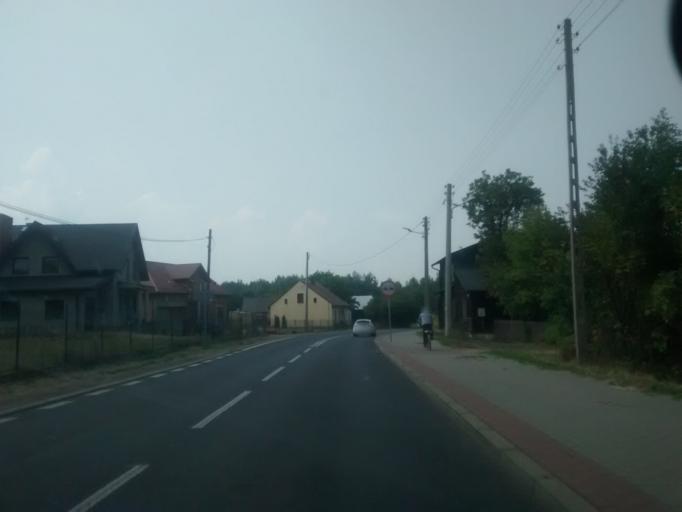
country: PL
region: Silesian Voivodeship
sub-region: Powiat czestochowski
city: Potok Zloty
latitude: 50.7239
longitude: 19.4245
